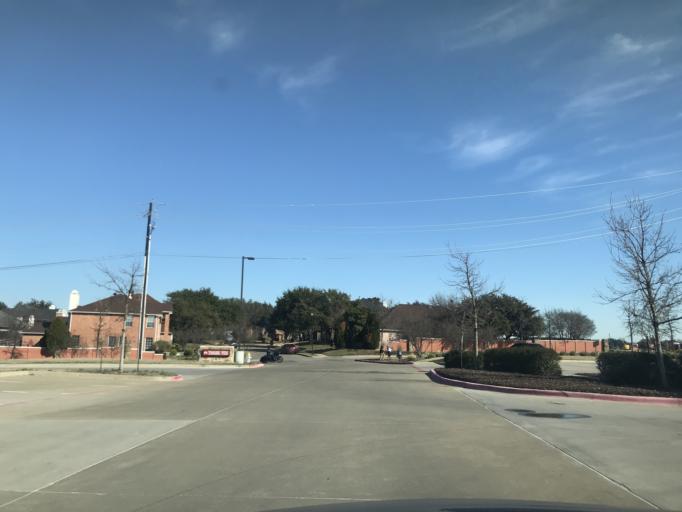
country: US
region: Texas
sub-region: Dallas County
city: Carrollton
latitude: 32.9860
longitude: -96.8982
